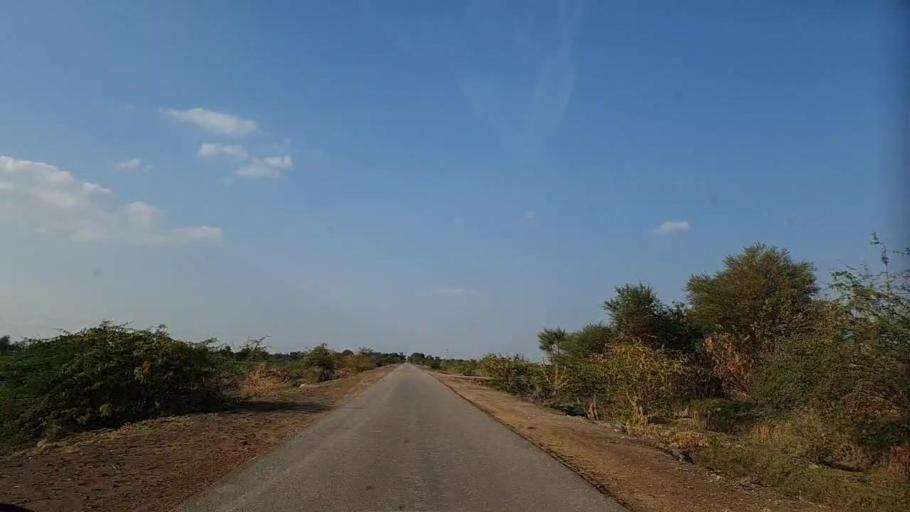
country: PK
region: Sindh
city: Pithoro
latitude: 25.7210
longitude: 69.2166
